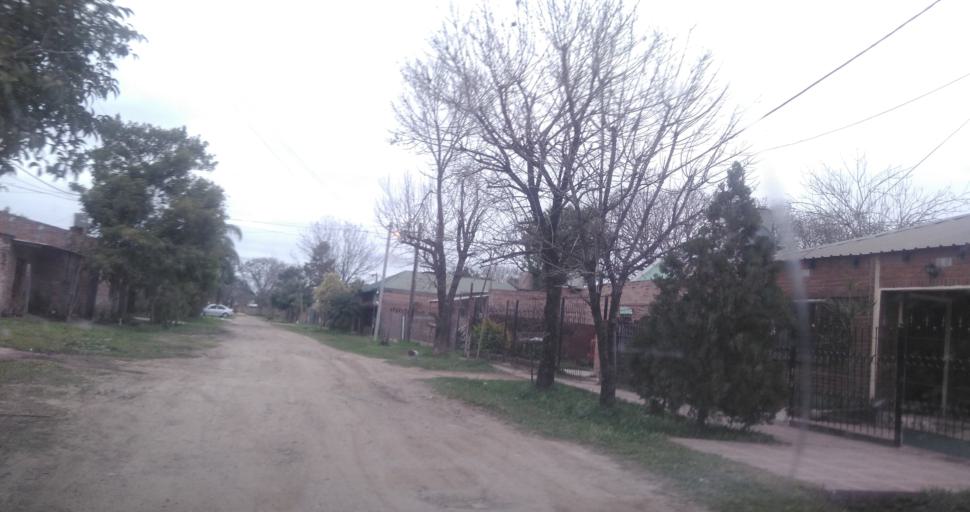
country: AR
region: Chaco
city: Fontana
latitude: -27.4437
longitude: -59.0351
